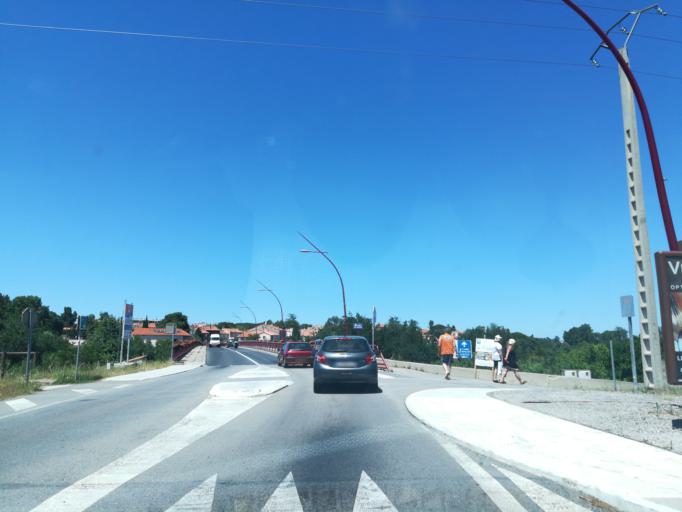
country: FR
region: Languedoc-Roussillon
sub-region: Departement des Pyrenees-Orientales
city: el Volo
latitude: 42.5178
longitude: 2.8321
